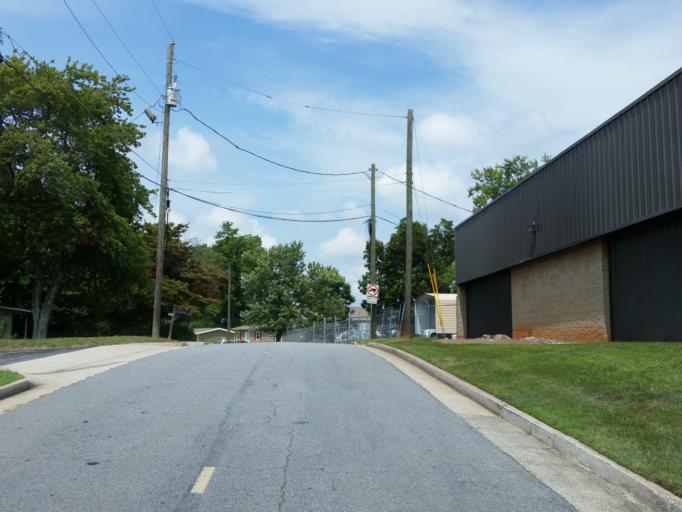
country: US
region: Georgia
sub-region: Cobb County
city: Marietta
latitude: 33.9427
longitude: -84.5187
